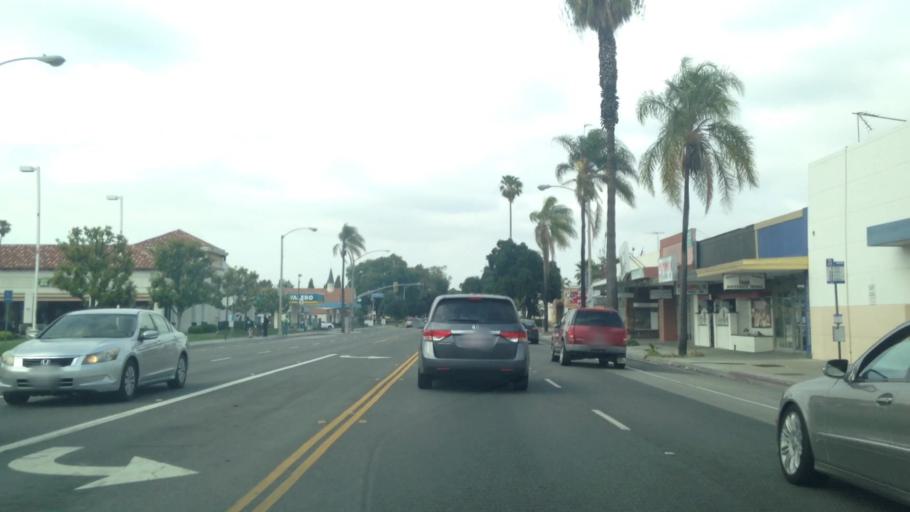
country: US
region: California
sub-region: Riverside County
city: Riverside
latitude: 33.9595
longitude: -117.3927
